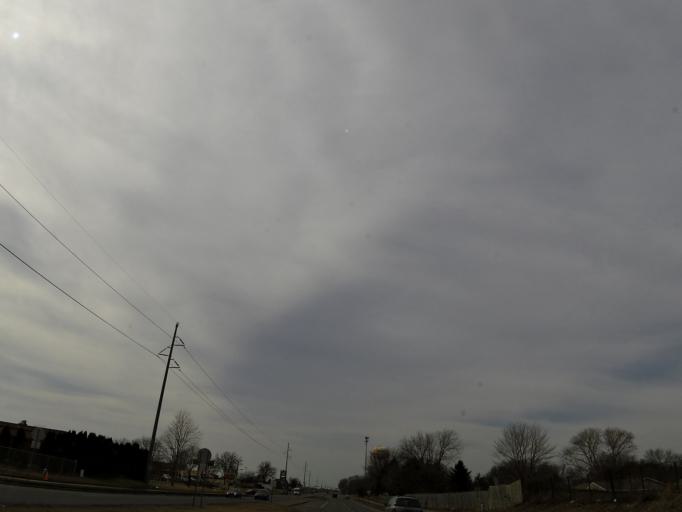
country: US
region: Minnesota
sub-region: Dakota County
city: Rosemount
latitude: 44.7319
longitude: -93.1295
